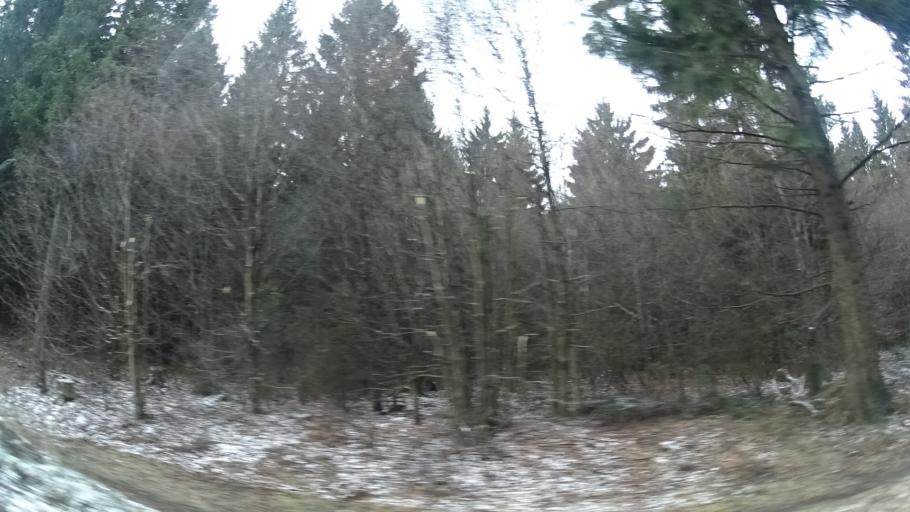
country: DE
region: Thuringia
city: Tabarz
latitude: 50.8393
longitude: 10.5192
